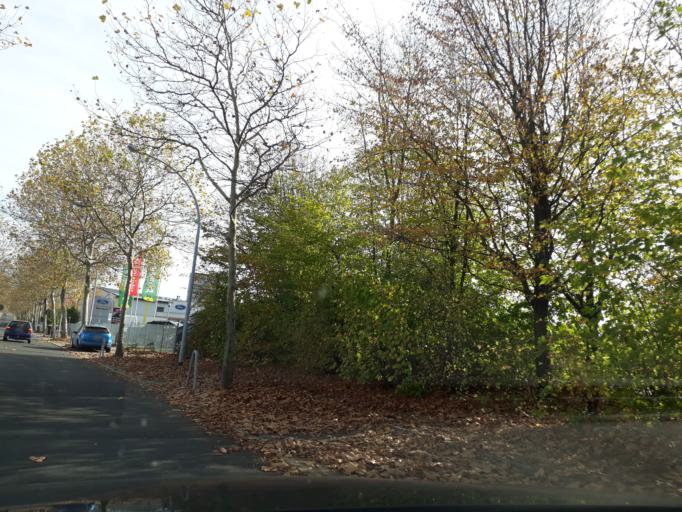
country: DE
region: Saxony
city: Niederstriegis
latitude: 51.1173
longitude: 13.1483
